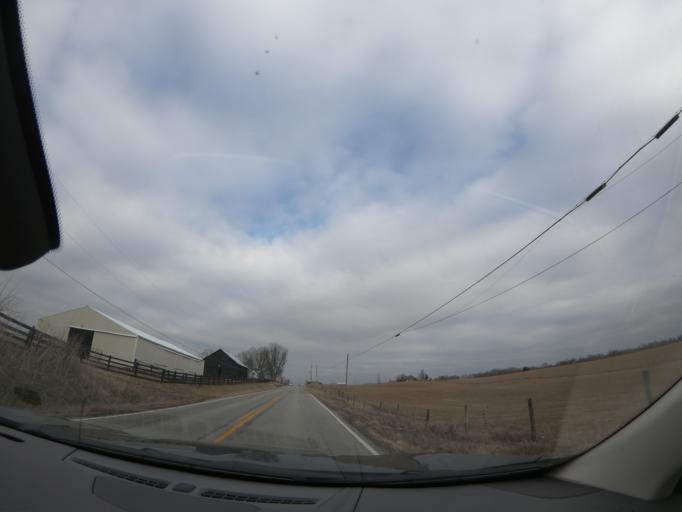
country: US
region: Kentucky
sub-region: Spencer County
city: Taylorsville
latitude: 37.8717
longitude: -85.3166
